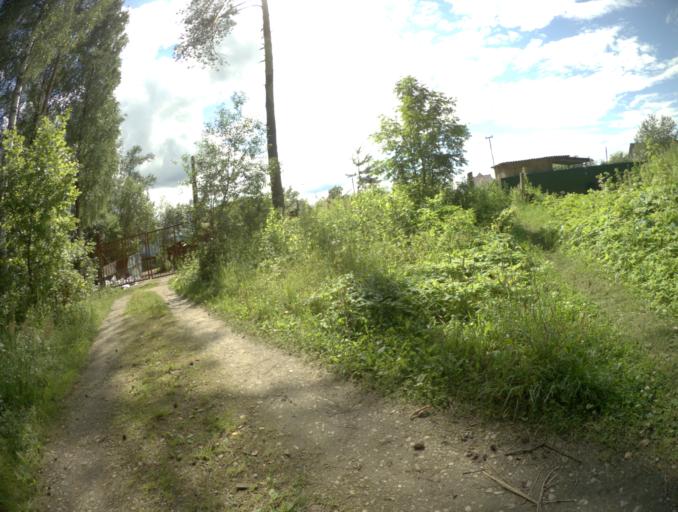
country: RU
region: Vladimir
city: Kommunar
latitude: 56.0488
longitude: 40.4502
